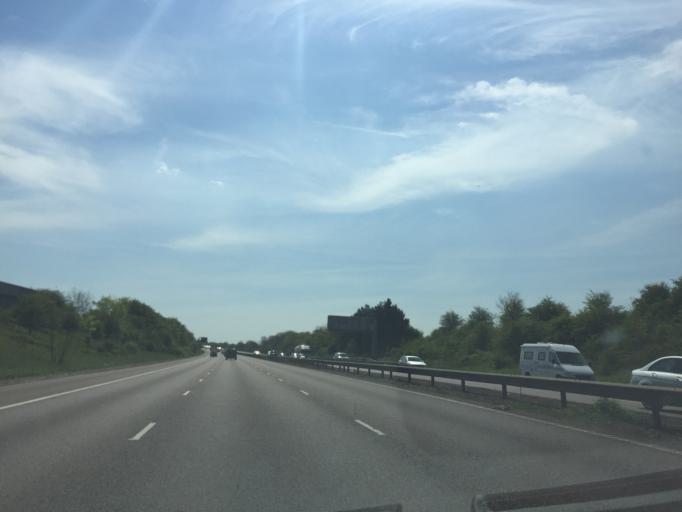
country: GB
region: England
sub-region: Essex
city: Epping
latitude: 51.7216
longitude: 0.1420
